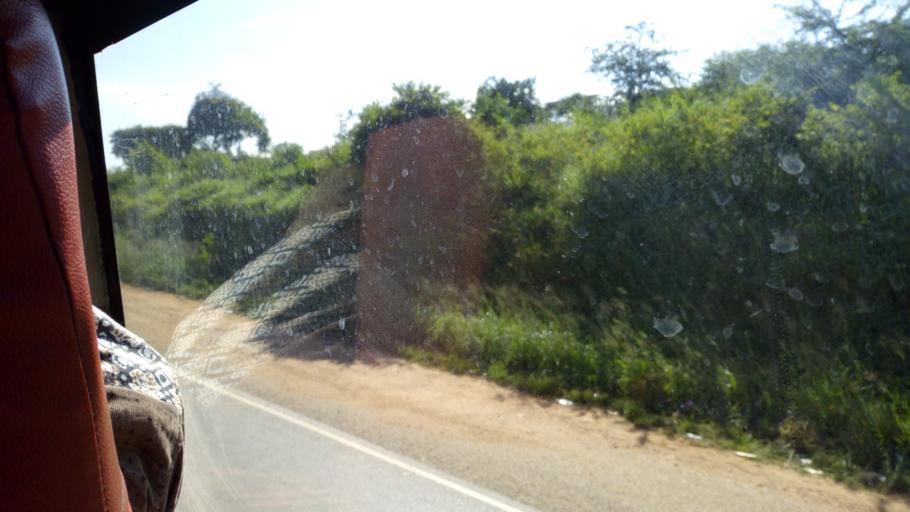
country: UG
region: Western Region
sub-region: Mbarara District
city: Mbarara
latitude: -0.4970
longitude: 30.8529
